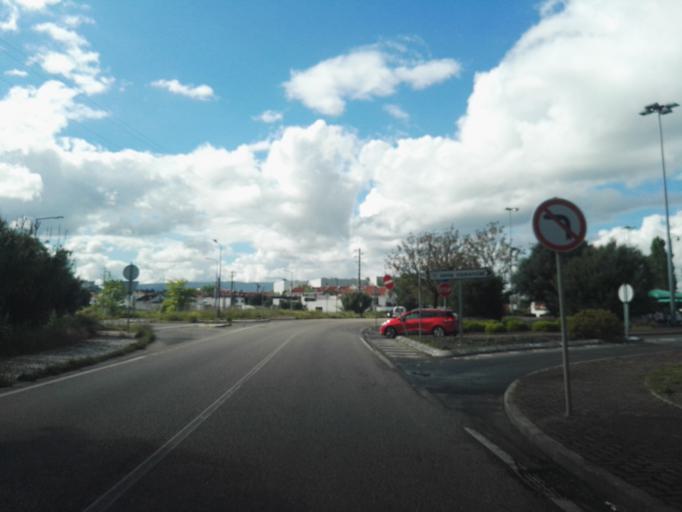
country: PT
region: Santarem
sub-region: Torres Novas
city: Riachos
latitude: 39.4621
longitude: -8.5215
